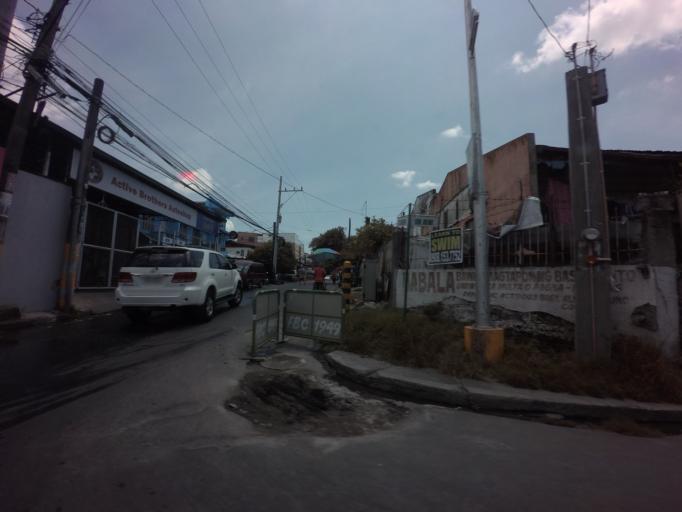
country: PH
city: Sambayanihan People's Village
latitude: 14.4282
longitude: 121.0146
